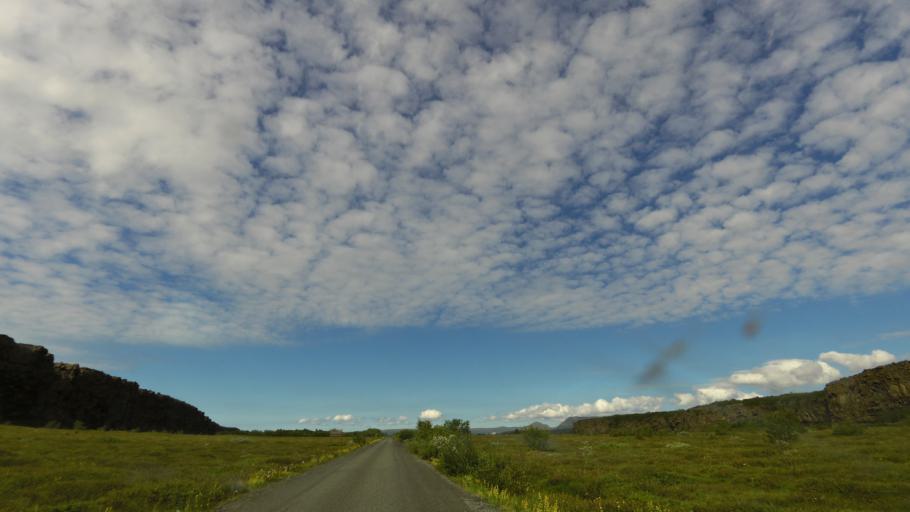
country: IS
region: Northeast
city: Husavik
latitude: 66.0189
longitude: -16.4967
